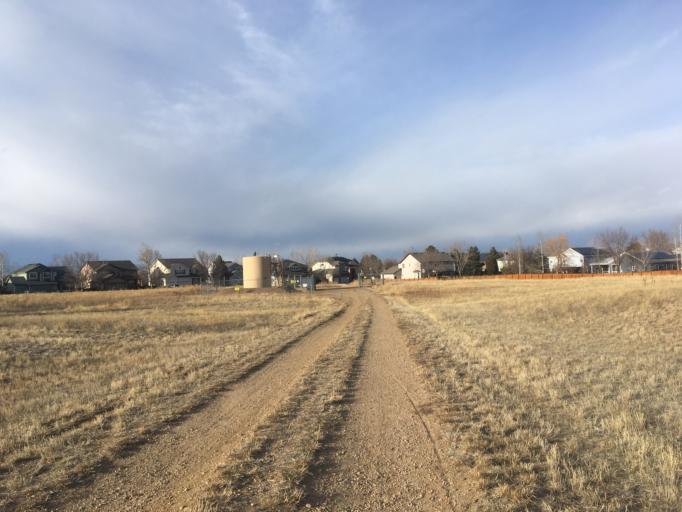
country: US
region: Colorado
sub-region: Boulder County
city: Lafayette
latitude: 40.0158
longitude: -105.0862
